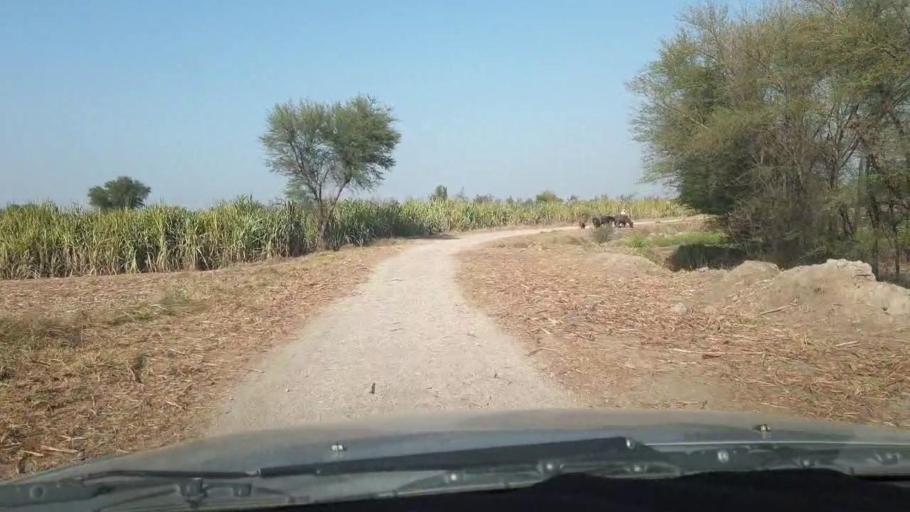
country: PK
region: Sindh
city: Mirpur Mathelo
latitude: 27.9207
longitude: 69.5571
